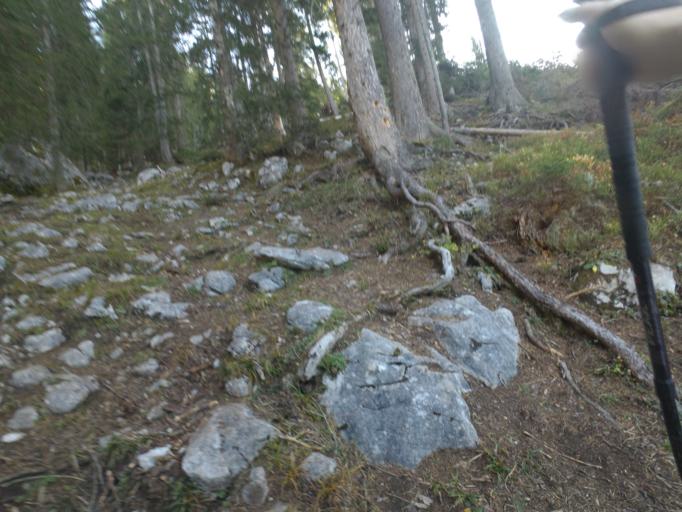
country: AT
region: Salzburg
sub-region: Politischer Bezirk Sankt Johann im Pongau
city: Werfenweng
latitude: 47.4881
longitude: 13.2299
